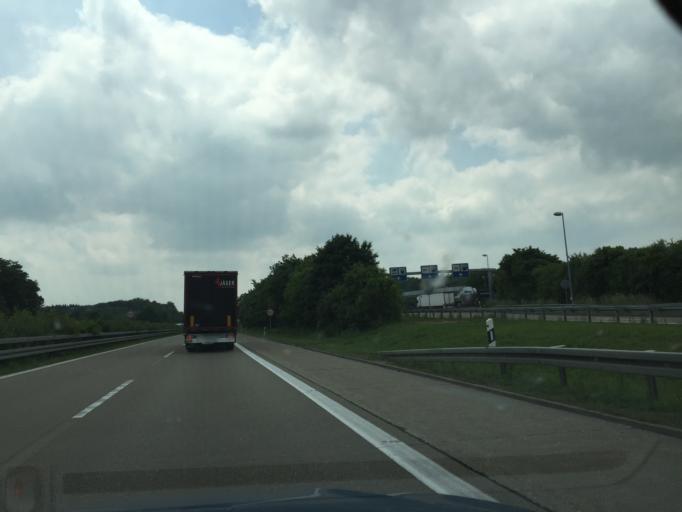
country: DE
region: Baden-Wuerttemberg
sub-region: Regierungsbezirk Stuttgart
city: Herbrechtingen
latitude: 48.5860
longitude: 10.1796
